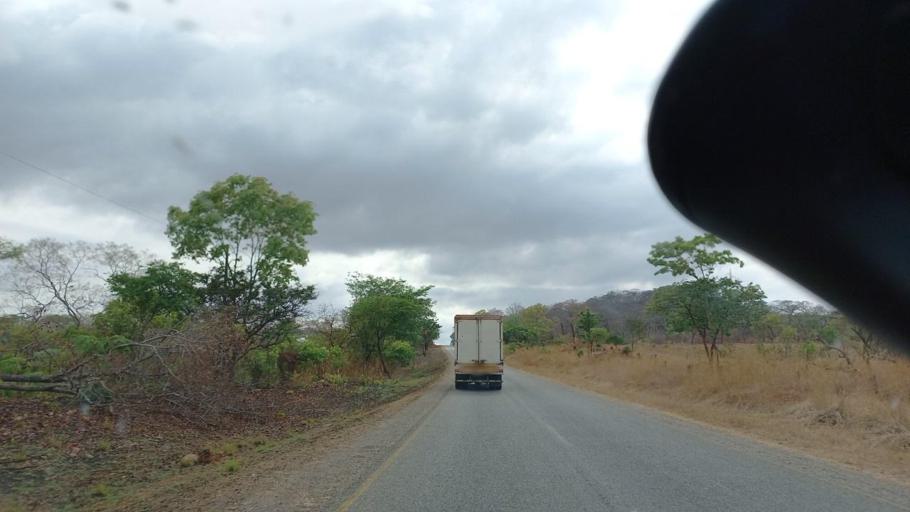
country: ZM
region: Lusaka
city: Chongwe
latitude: -15.1316
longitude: 29.5190
